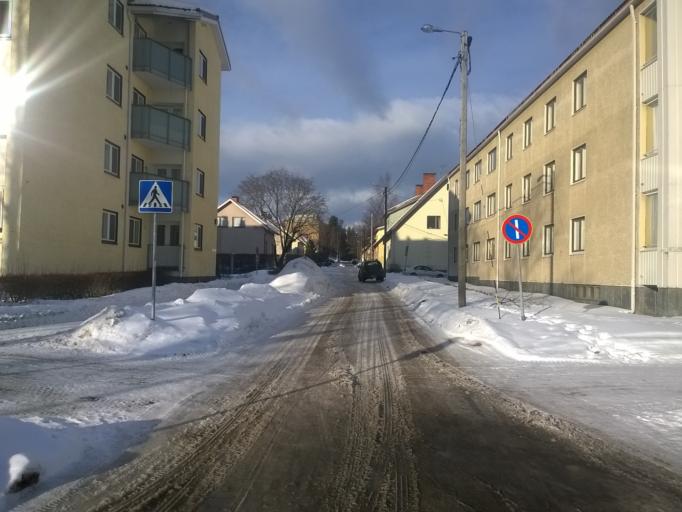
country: FI
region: Southern Savonia
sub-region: Mikkeli
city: Mikkeli
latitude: 61.6839
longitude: 27.2561
